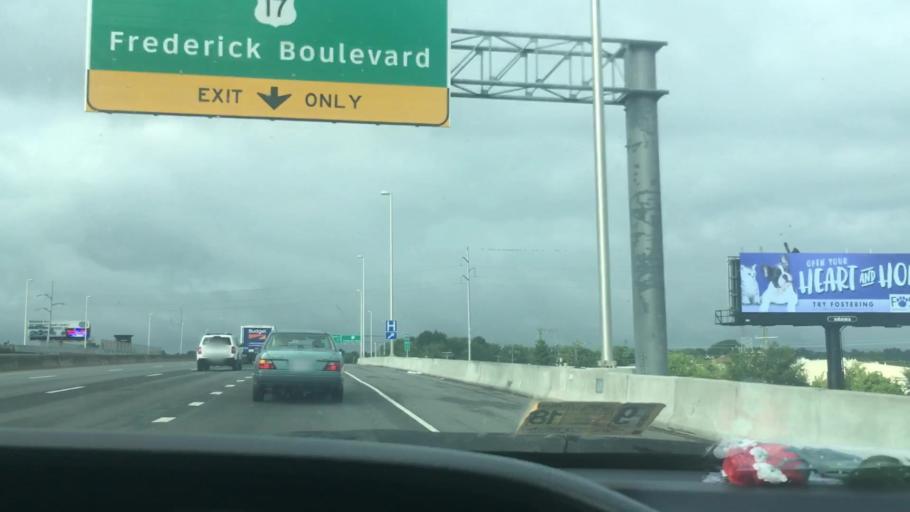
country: US
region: Virginia
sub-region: City of Portsmouth
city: Portsmouth
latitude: 36.8251
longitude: -76.3283
